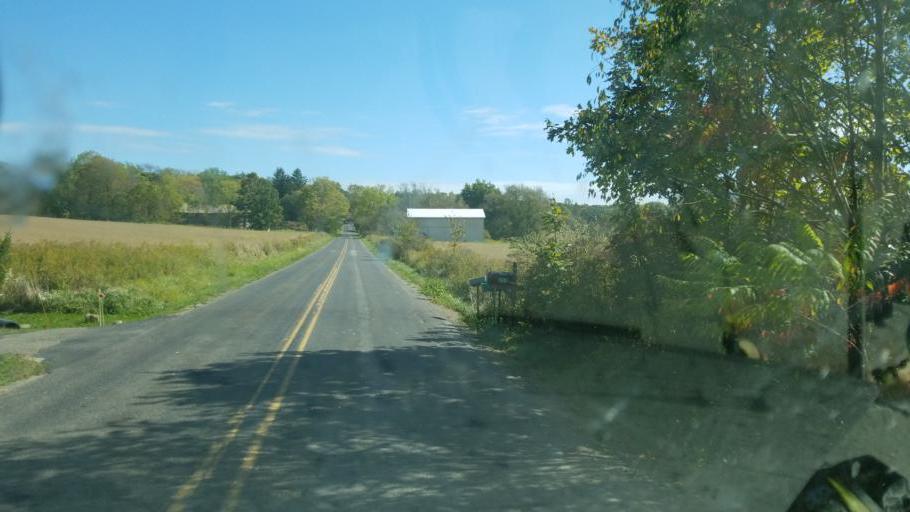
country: US
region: Pennsylvania
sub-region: Mercer County
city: Greenville
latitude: 41.3862
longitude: -80.4342
